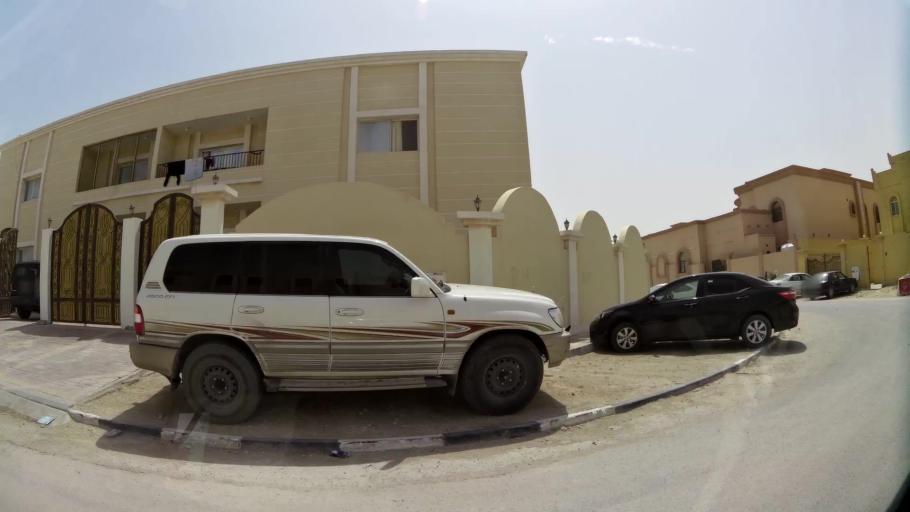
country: QA
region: Baladiyat ar Rayyan
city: Ar Rayyan
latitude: 25.2367
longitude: 51.4160
